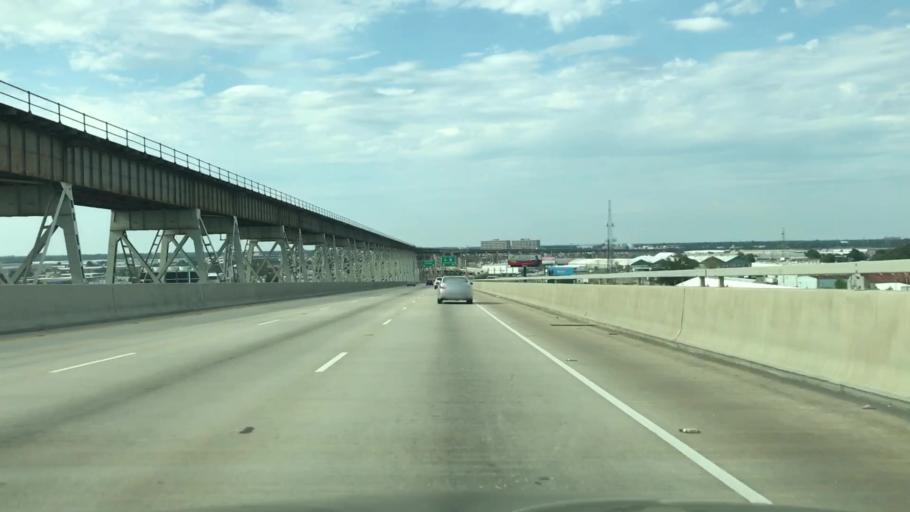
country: US
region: Louisiana
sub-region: Jefferson Parish
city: Bridge City
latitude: 29.9484
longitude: -90.1734
